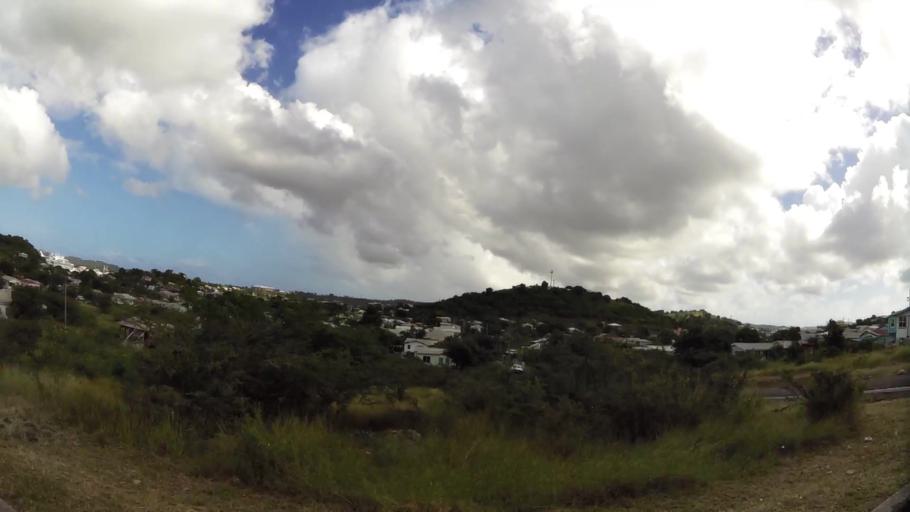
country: AG
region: Saint John
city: Saint John's
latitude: 17.1114
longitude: -61.8564
